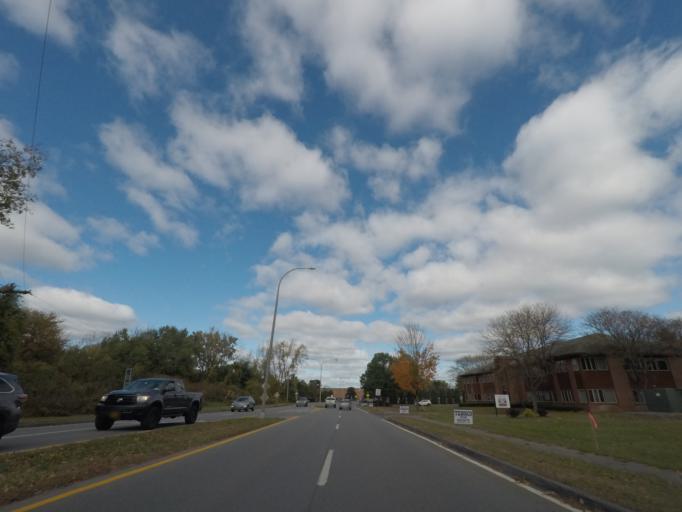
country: US
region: New York
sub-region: Saratoga County
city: Country Knolls
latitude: 42.8556
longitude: -73.7832
